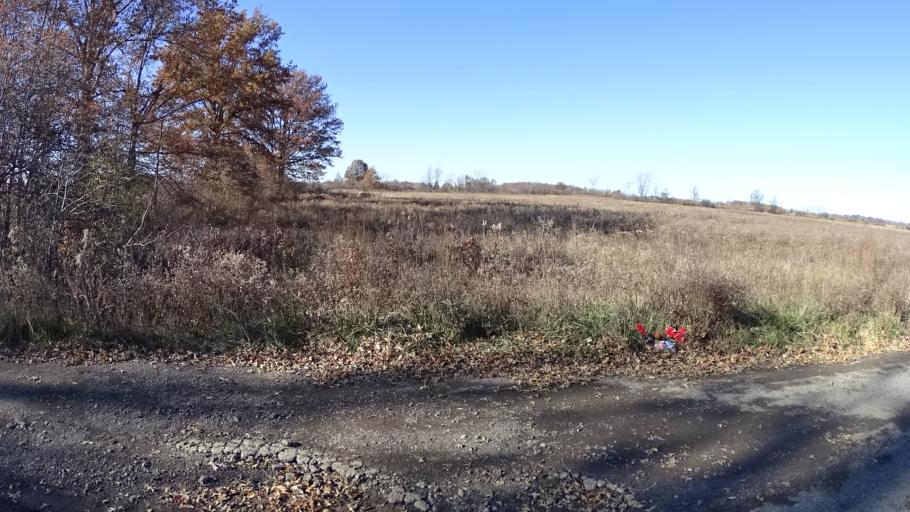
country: US
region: Ohio
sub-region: Lorain County
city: Elyria
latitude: 41.3607
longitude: -82.1655
